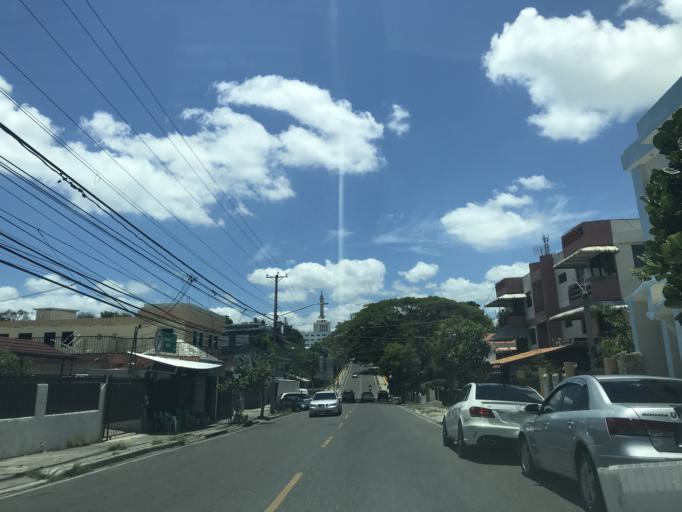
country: DO
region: Santiago
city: Santiago de los Caballeros
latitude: 19.4442
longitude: -70.6979
